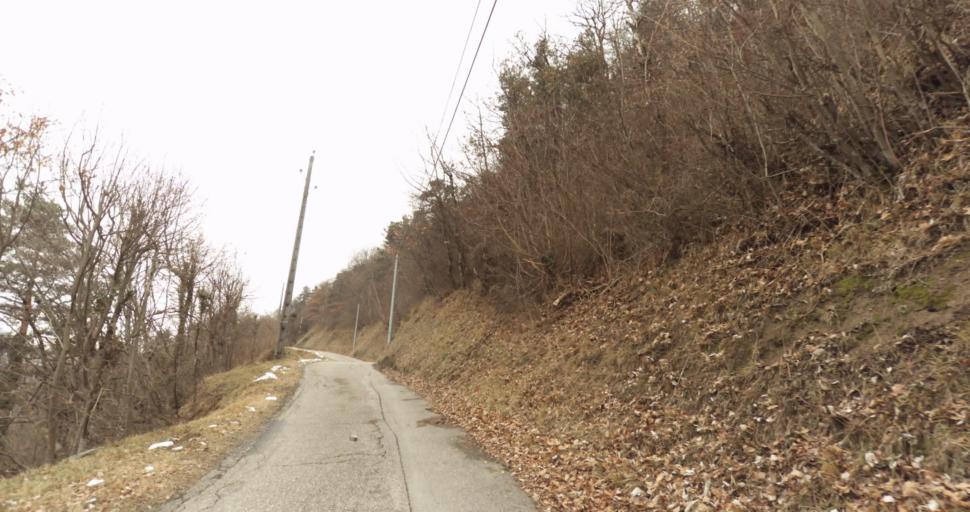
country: FR
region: Rhone-Alpes
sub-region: Departement de l'Isere
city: Saint-Georges-de-Commiers
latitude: 45.0111
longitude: 5.6810
